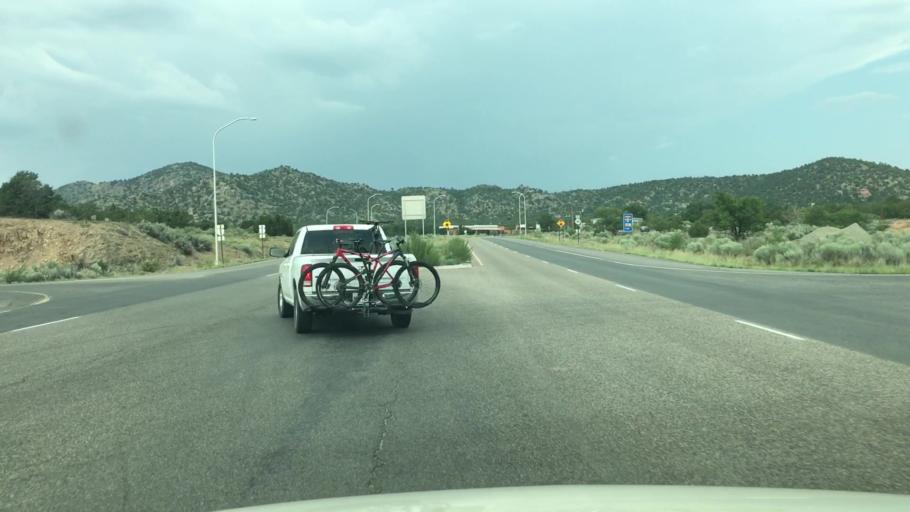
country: US
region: New Mexico
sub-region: Santa Fe County
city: Eldorado at Santa Fe
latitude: 35.5556
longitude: -105.8783
